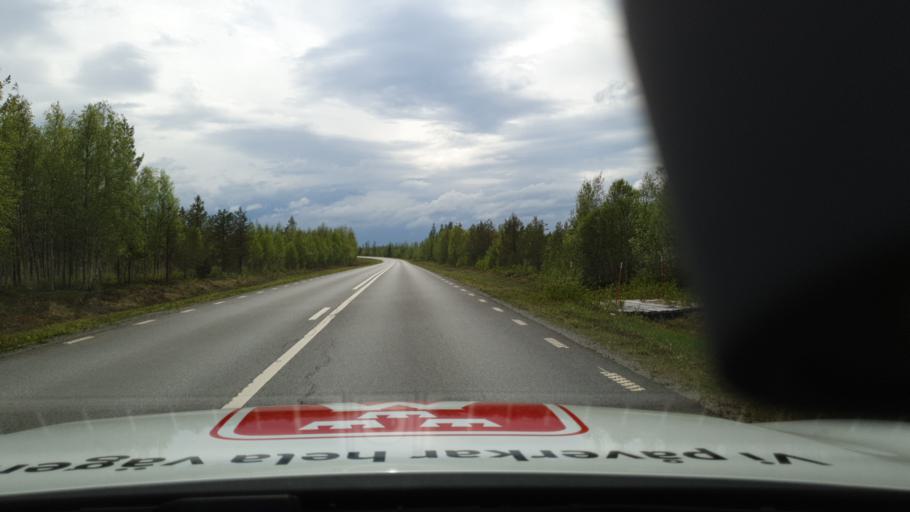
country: SE
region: Vaesterbotten
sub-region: Dorotea Kommun
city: Dorotea
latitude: 64.3229
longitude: 16.6185
